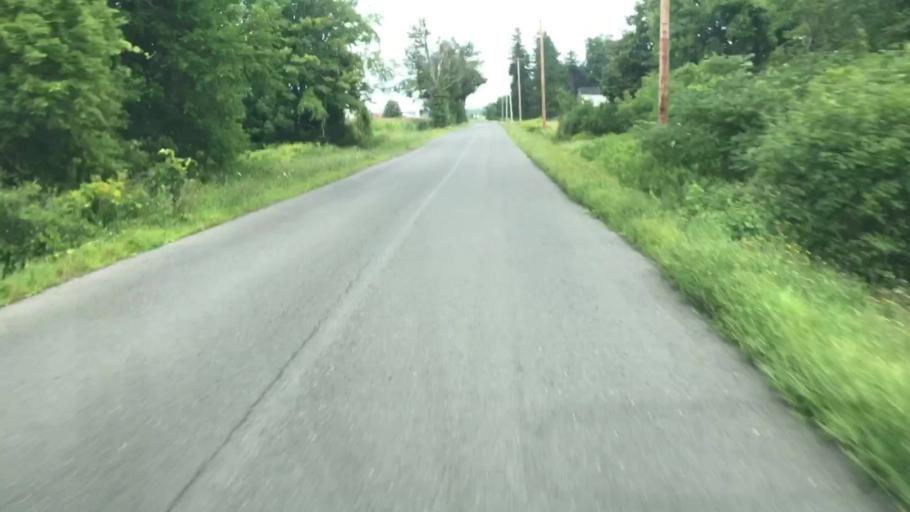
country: US
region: New York
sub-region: Onondaga County
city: Elbridge
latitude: 42.9860
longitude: -76.4804
